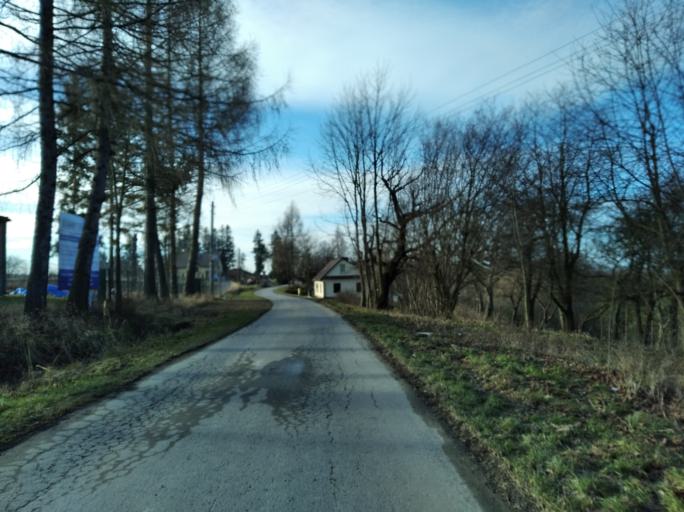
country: PL
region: Subcarpathian Voivodeship
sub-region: Powiat strzyzowski
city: Gwoznica Gorna
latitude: 49.8265
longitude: 21.9635
